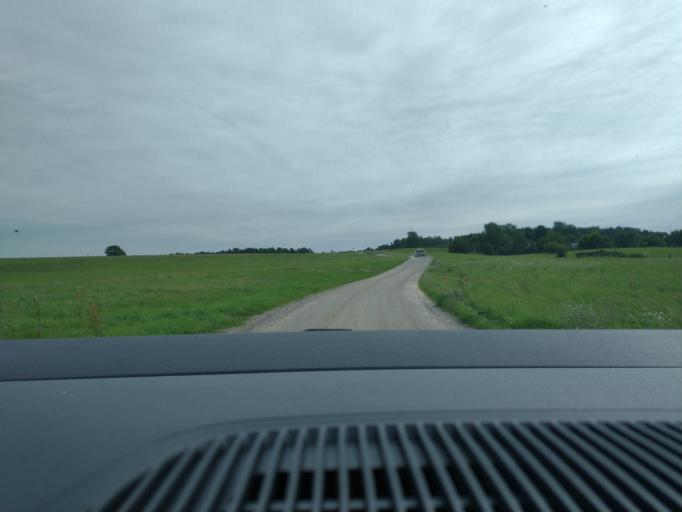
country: SE
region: Skane
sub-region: Lunds Kommun
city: Veberod
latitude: 55.6889
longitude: 13.4971
